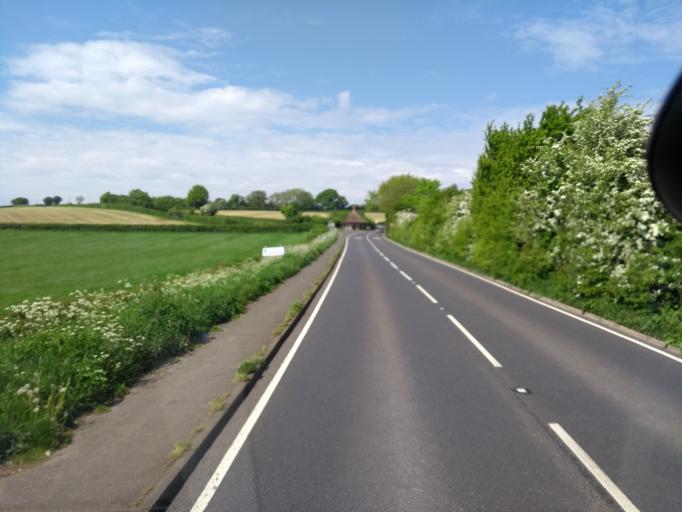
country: GB
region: England
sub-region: Somerset
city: Chard
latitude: 50.8736
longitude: -2.9757
